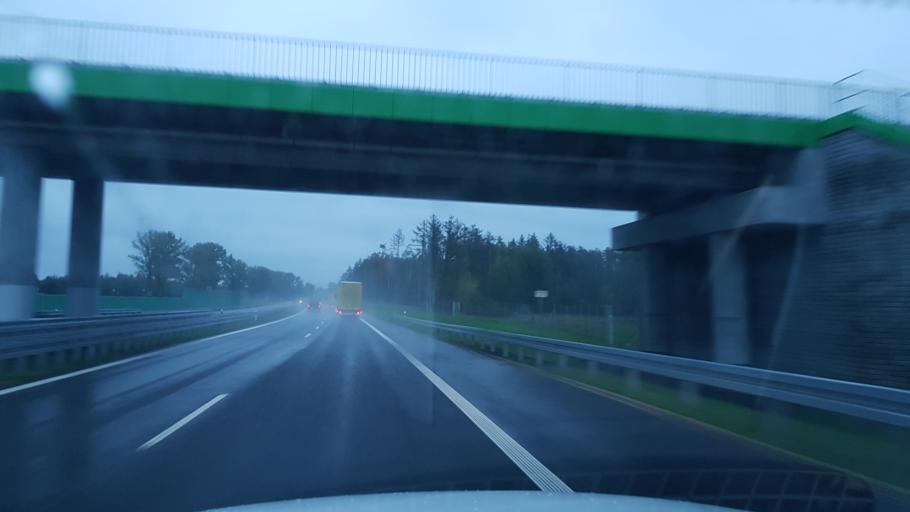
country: PL
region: West Pomeranian Voivodeship
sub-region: Powiat gryficki
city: Ploty
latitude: 53.8553
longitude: 15.3429
